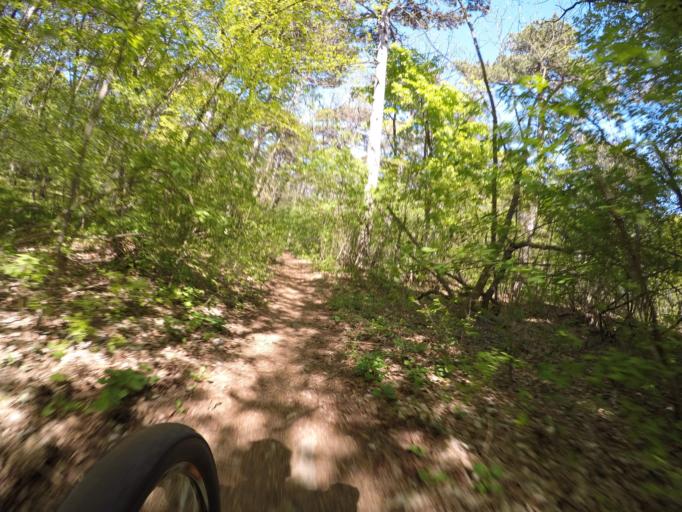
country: AT
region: Lower Austria
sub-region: Politischer Bezirk Modling
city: Gumpoldskirchen
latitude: 48.0642
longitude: 16.2810
